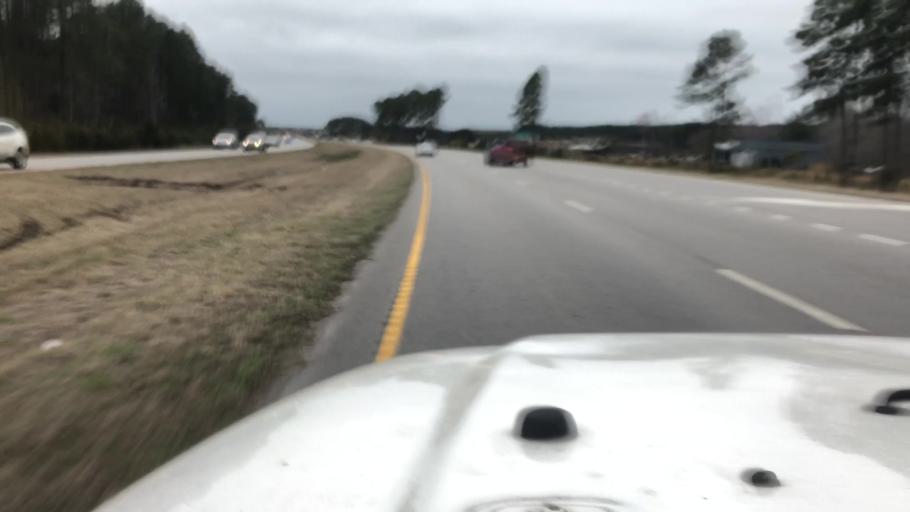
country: US
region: South Carolina
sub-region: Beaufort County
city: Bluffton
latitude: 32.2974
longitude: -80.9421
